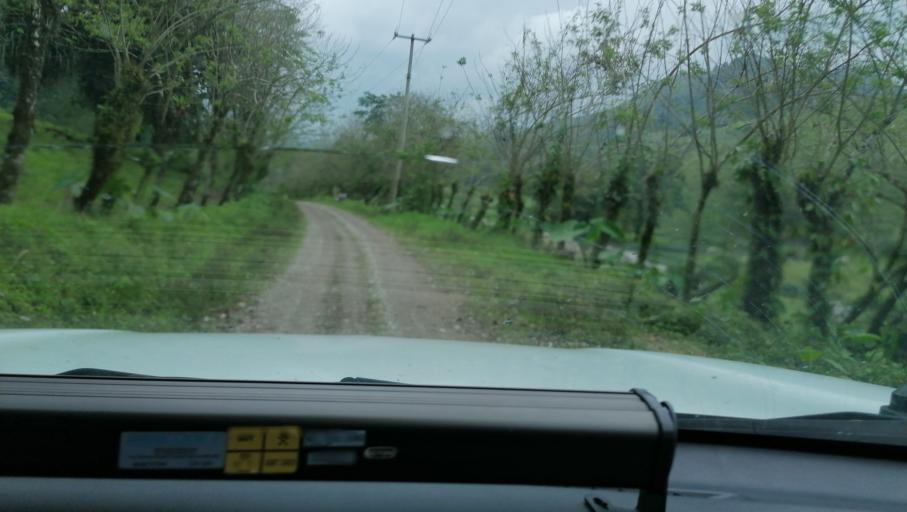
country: MX
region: Chiapas
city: Ixtacomitan
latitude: 17.3529
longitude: -93.1629
